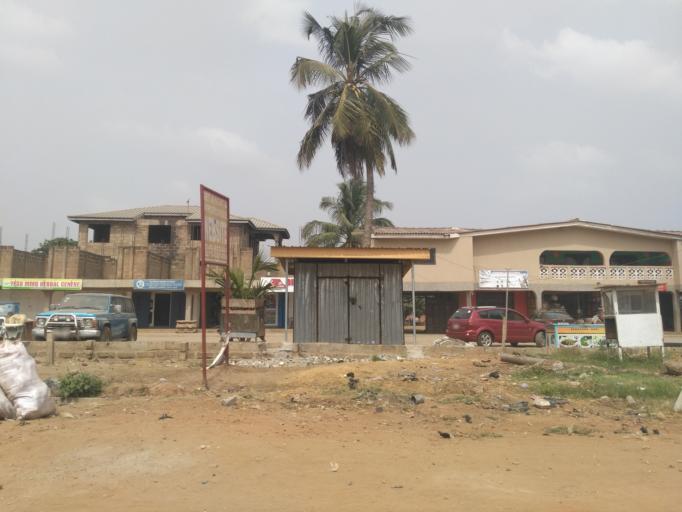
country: GH
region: Greater Accra
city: Nungua
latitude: 5.5967
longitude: -0.0832
